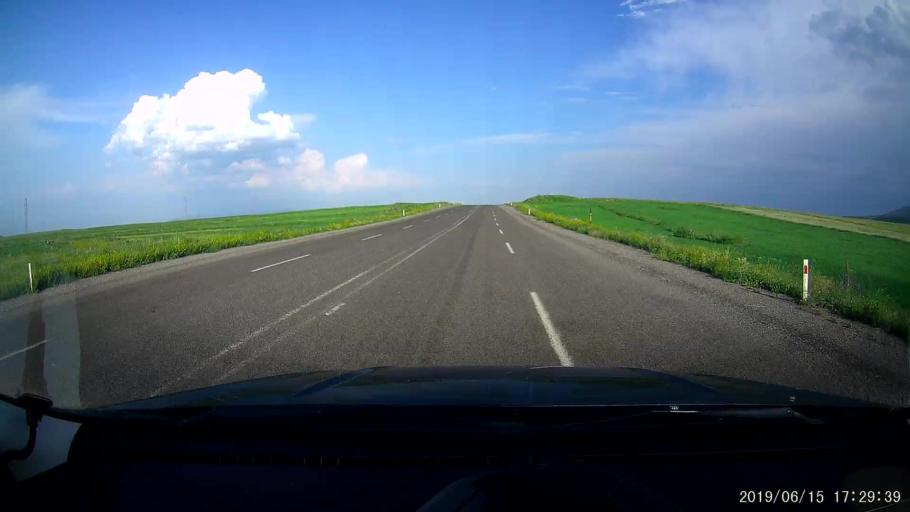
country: TR
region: Kars
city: Basgedikler
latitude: 40.5882
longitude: 43.4558
